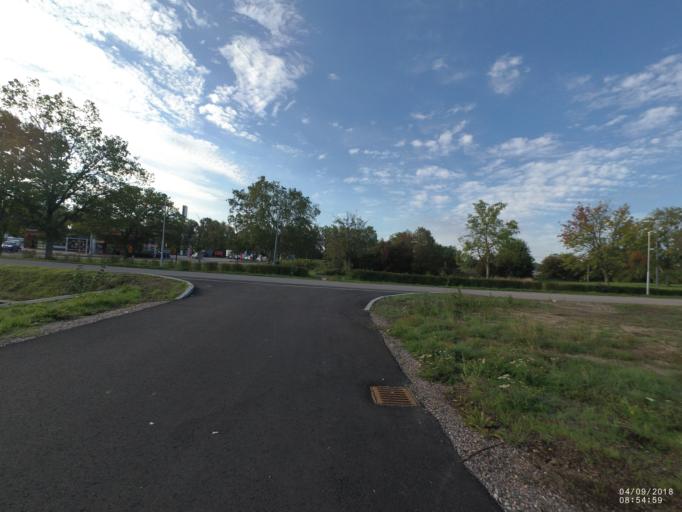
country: SE
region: Soedermanland
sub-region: Nykopings Kommun
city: Nykoping
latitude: 58.7507
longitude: 16.9859
